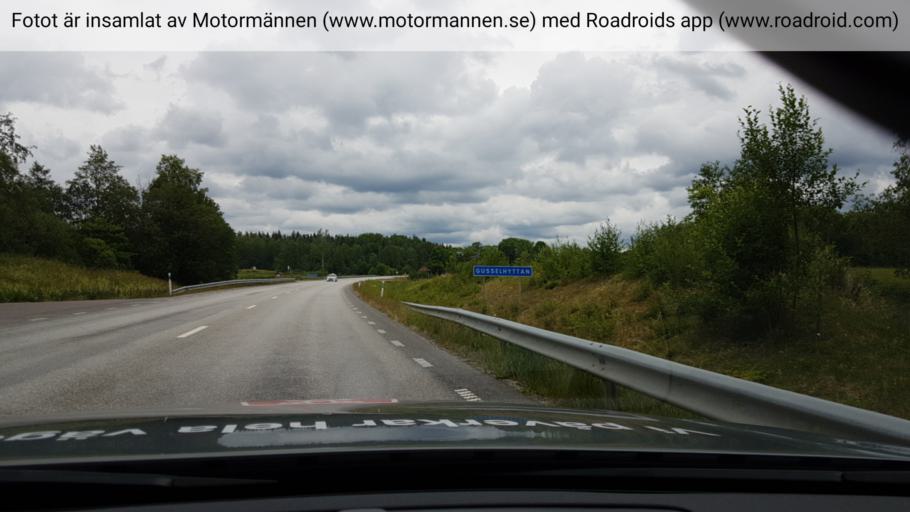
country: SE
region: OErebro
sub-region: Lindesbergs Kommun
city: Lindesberg
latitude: 59.6440
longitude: 15.2330
